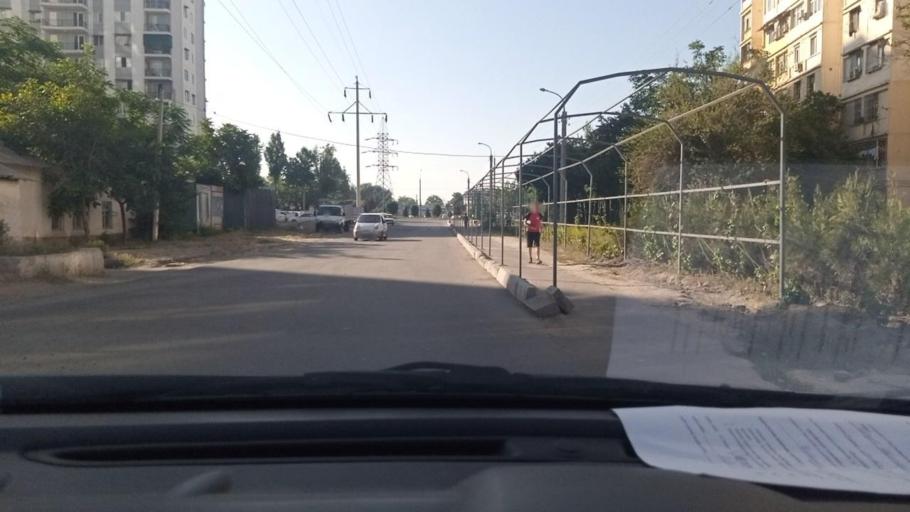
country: UZ
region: Toshkent
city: Salor
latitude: 41.3220
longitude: 69.3600
